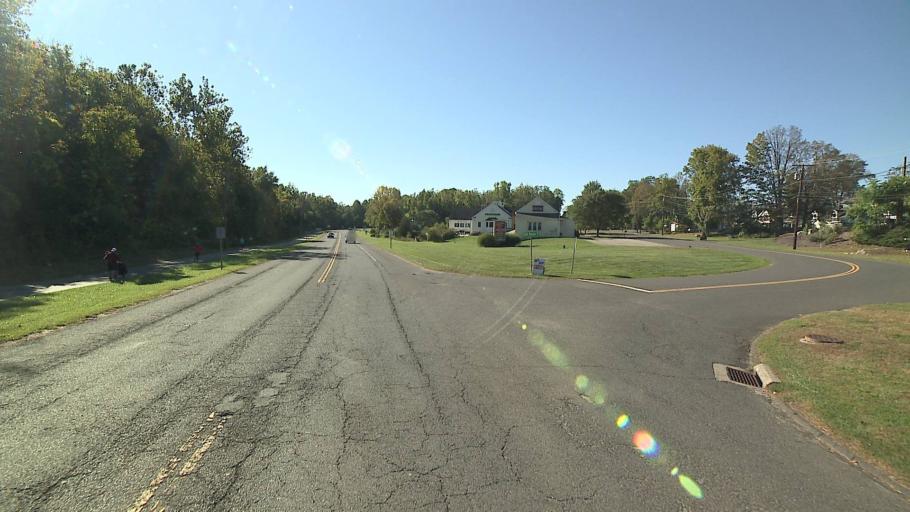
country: US
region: Connecticut
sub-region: Fairfield County
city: Danbury
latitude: 41.4782
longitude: -73.4085
